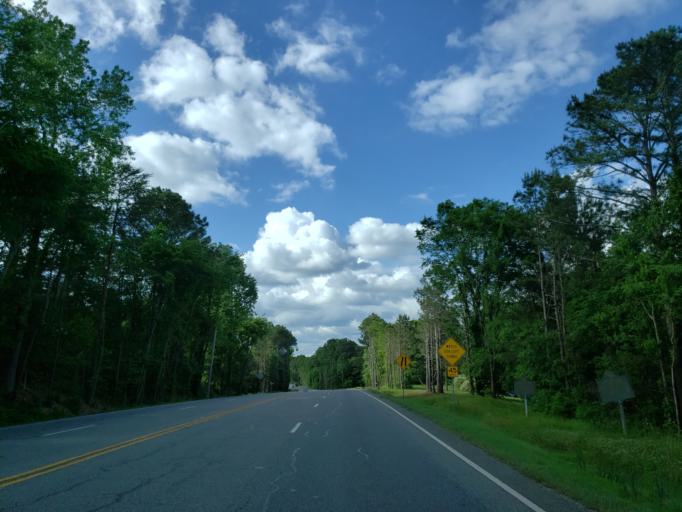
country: US
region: Georgia
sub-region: Bartow County
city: Cartersville
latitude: 34.2490
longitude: -84.8573
